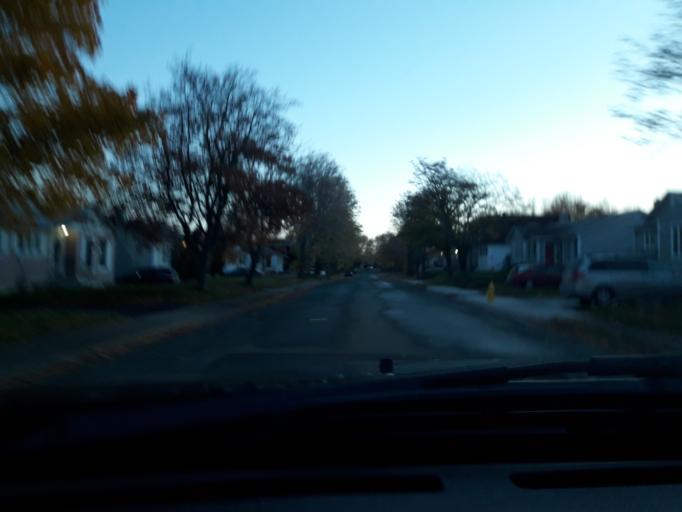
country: CA
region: Newfoundland and Labrador
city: St. John's
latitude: 47.5658
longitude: -52.7454
